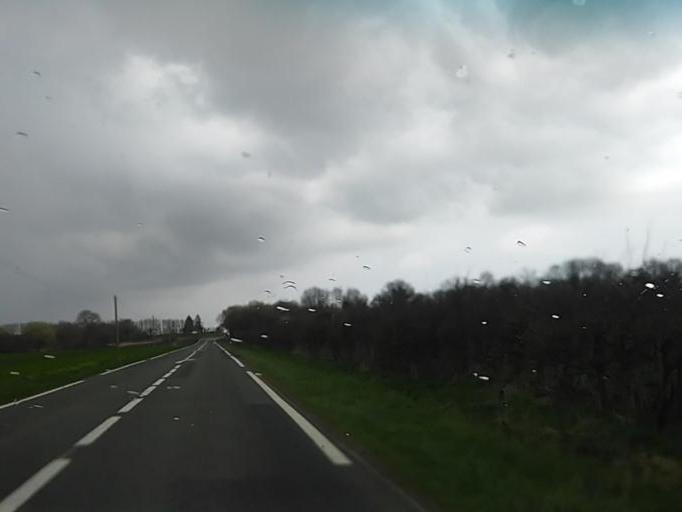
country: FR
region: Lower Normandy
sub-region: Departement du Calvados
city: Falaise
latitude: 48.8786
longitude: -0.2104
